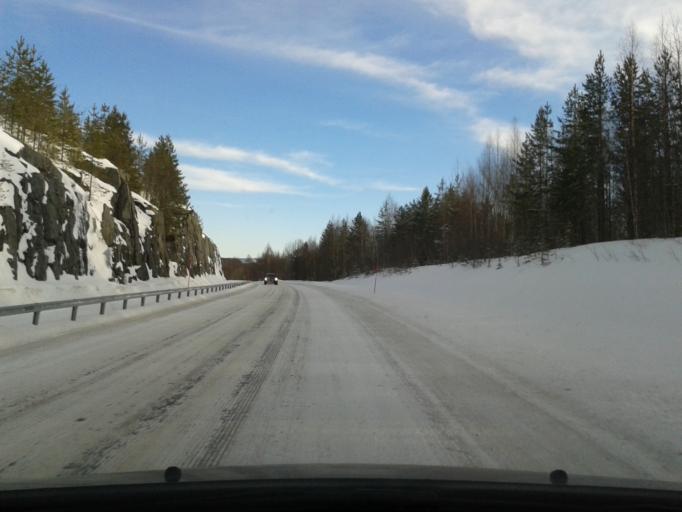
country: SE
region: Vaesterbotten
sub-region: Asele Kommun
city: Asele
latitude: 64.3235
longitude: 17.0737
